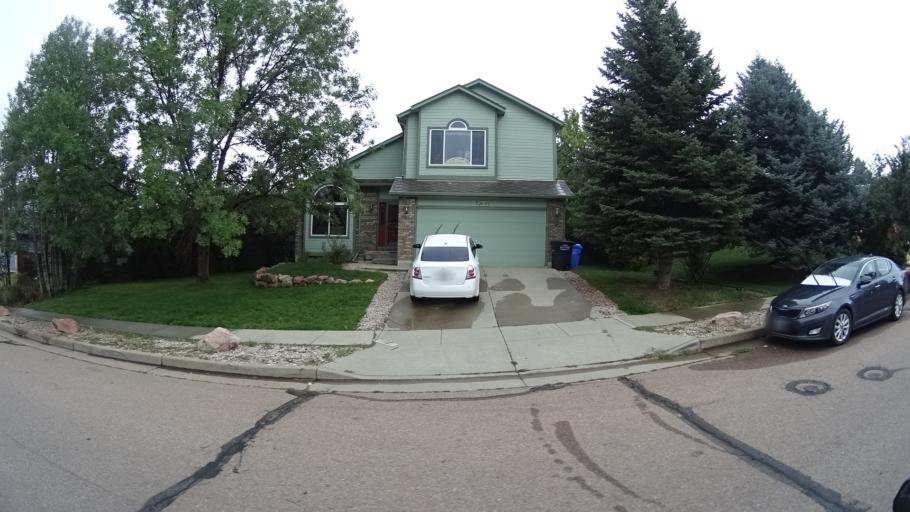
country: US
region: Colorado
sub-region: El Paso County
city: Cimarron Hills
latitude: 38.9192
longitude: -104.7594
